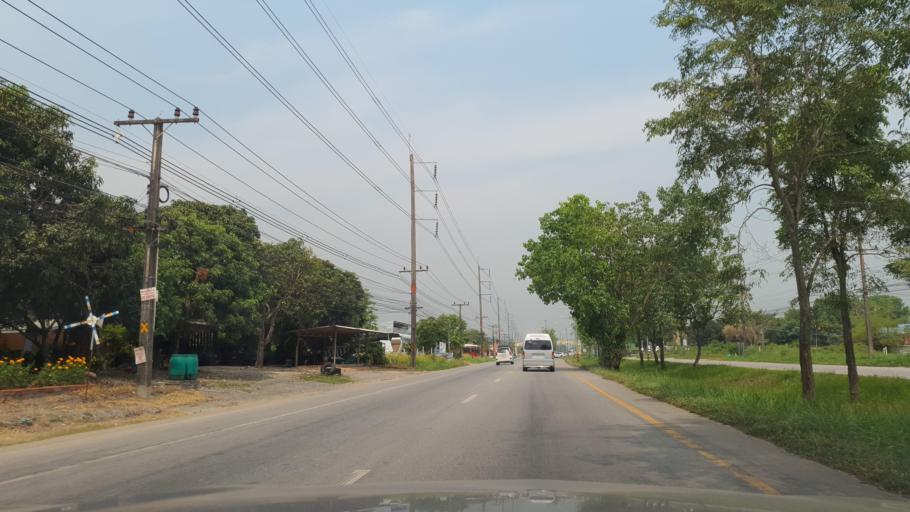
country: TH
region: Rayong
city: Rayong
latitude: 12.6407
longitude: 101.3978
